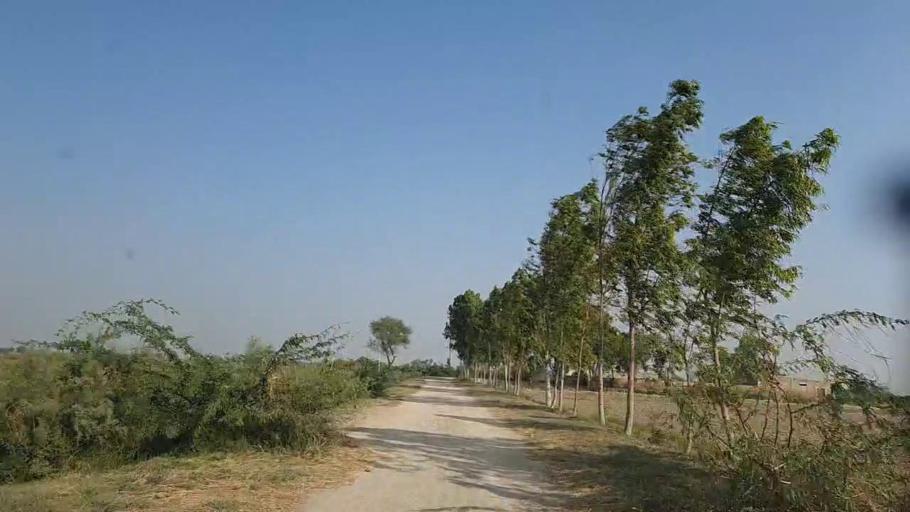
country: PK
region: Sindh
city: Mirpur Batoro
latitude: 24.5790
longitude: 68.2237
